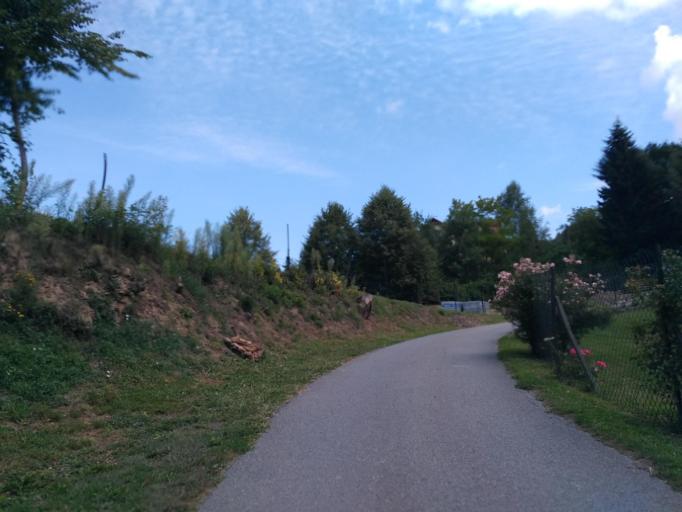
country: PL
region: Subcarpathian Voivodeship
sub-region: Powiat strzyzowski
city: Polomia
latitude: 49.9130
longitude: 21.8877
